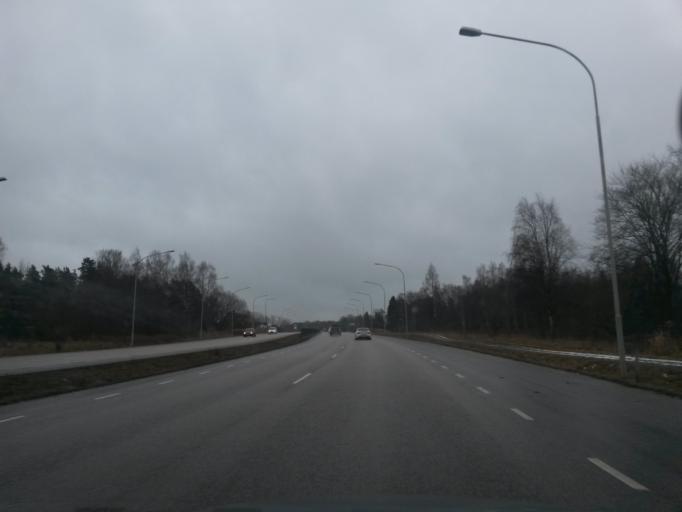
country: SE
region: Vaestra Goetaland
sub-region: Vanersborgs Kommun
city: Vanersborg
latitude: 58.3595
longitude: 12.3121
